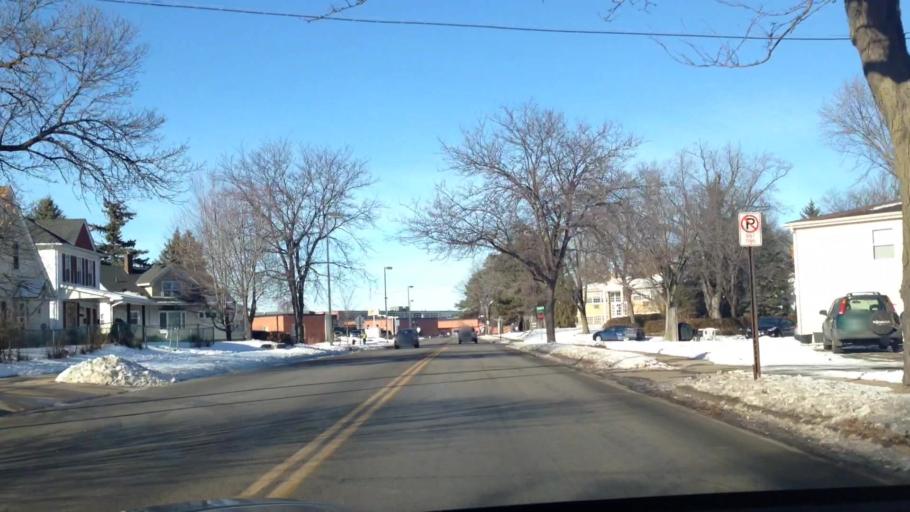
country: US
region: Minnesota
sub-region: Hennepin County
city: Saint Louis Park
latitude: 44.9405
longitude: -93.3582
